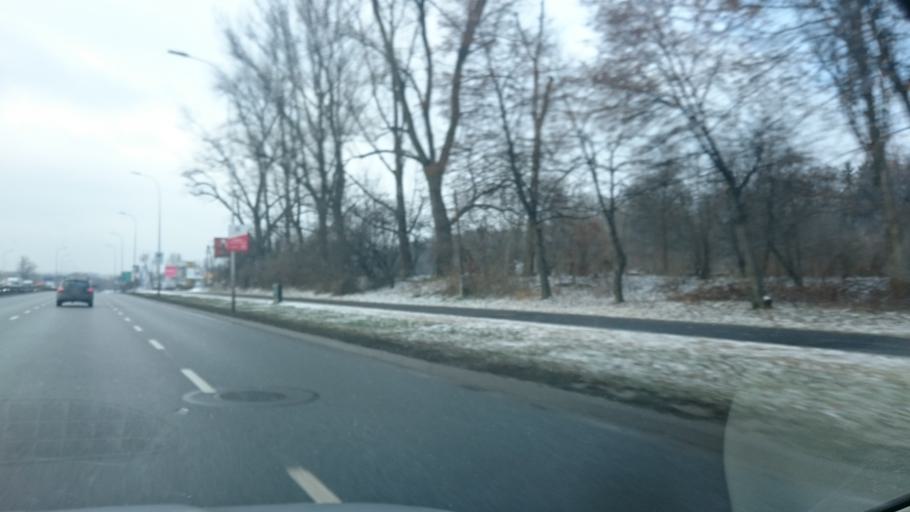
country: PL
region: Lesser Poland Voivodeship
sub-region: Krakow
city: Krakow
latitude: 50.0390
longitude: 19.9526
